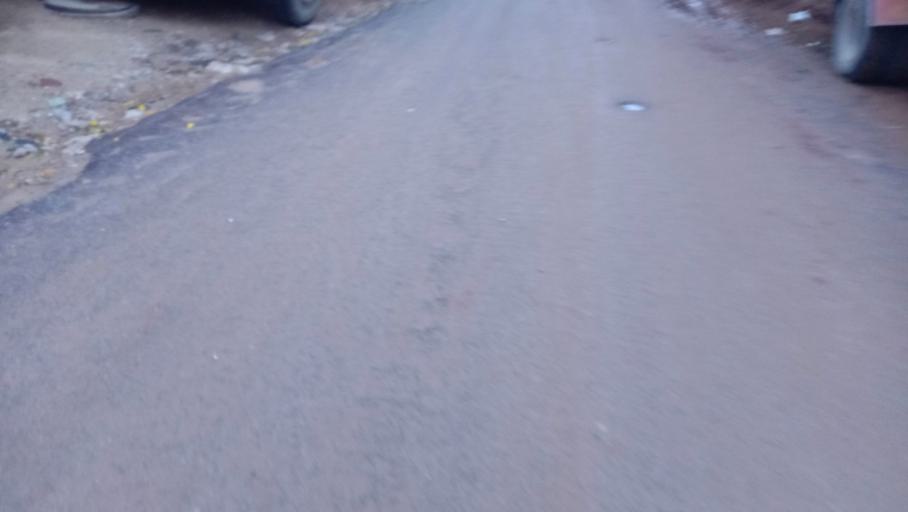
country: IN
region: Telangana
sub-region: Rangareddi
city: Kukatpalli
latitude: 17.4535
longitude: 78.3915
